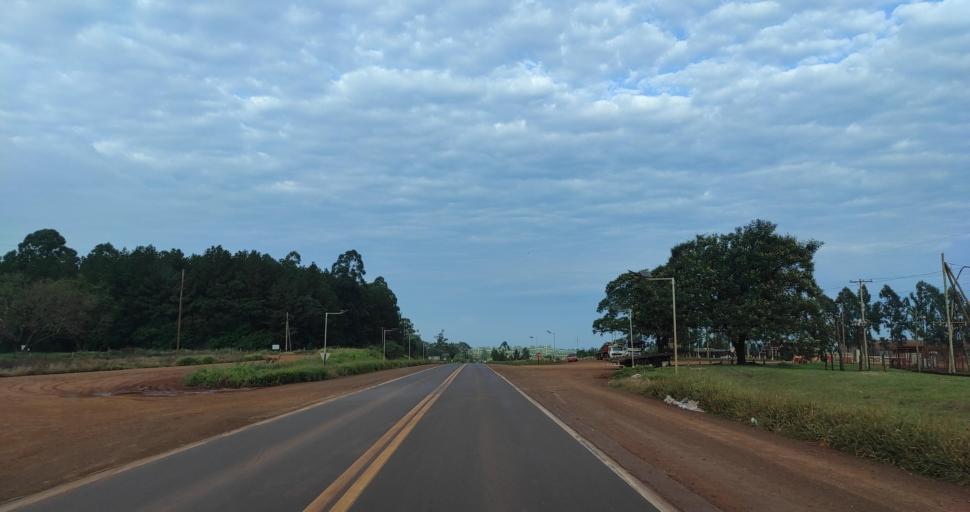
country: AR
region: Corrientes
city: Gobernador Ingeniero Valentin Virasoro
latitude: -27.9482
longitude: -55.9908
